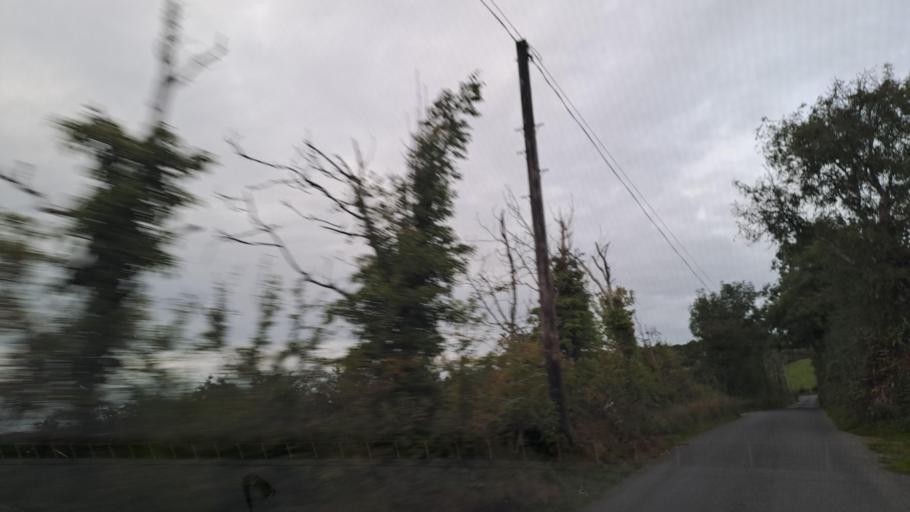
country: IE
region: Ulster
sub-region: An Cabhan
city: Kingscourt
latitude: 53.9869
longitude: -6.8621
